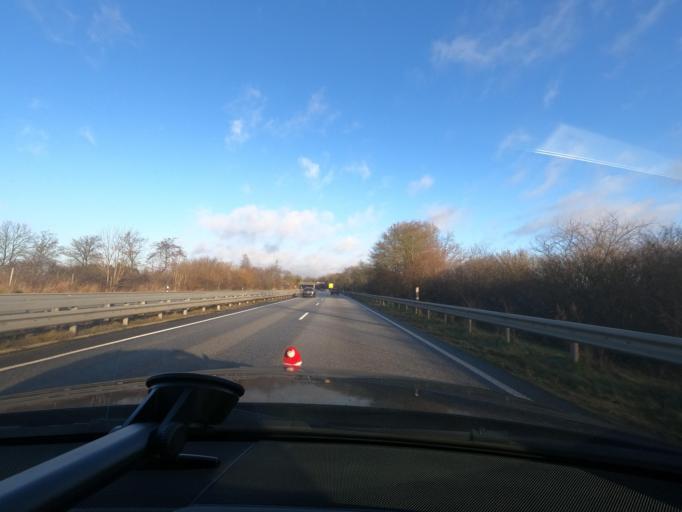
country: DE
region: Schleswig-Holstein
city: Jarplund-Weding
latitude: 54.7479
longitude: 9.4236
